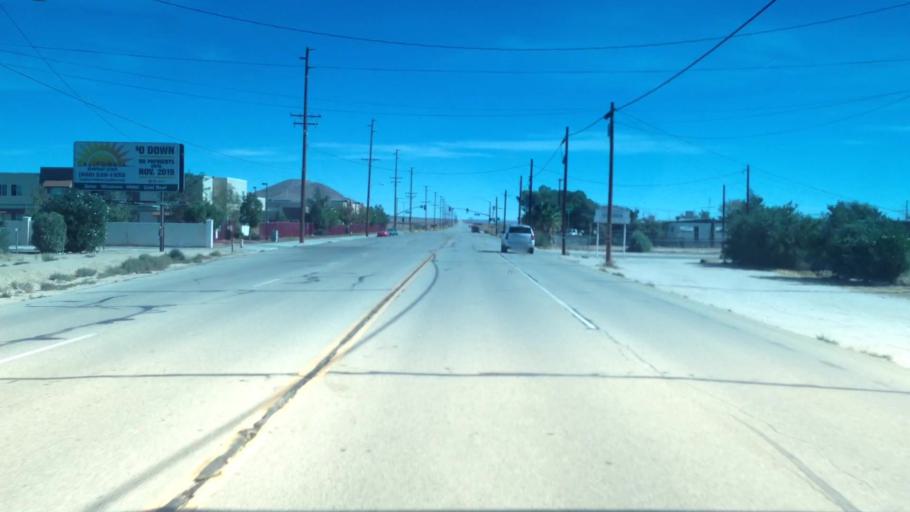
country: US
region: California
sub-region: Kern County
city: Rosamond
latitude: 34.8645
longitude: -118.1524
